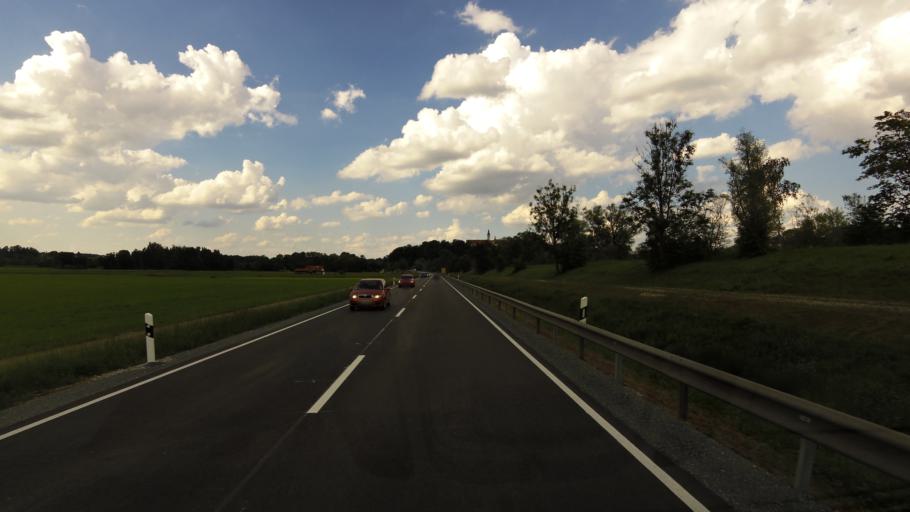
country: DE
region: Bavaria
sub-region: Upper Bavaria
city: Griesstatt
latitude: 48.0148
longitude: 12.1726
